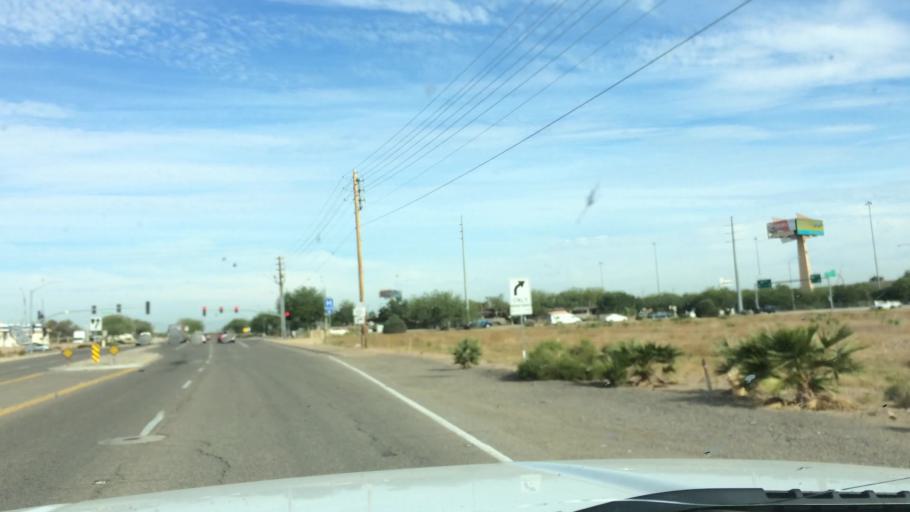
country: US
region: Arizona
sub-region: Maricopa County
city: Peoria
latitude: 33.5357
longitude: -112.2724
